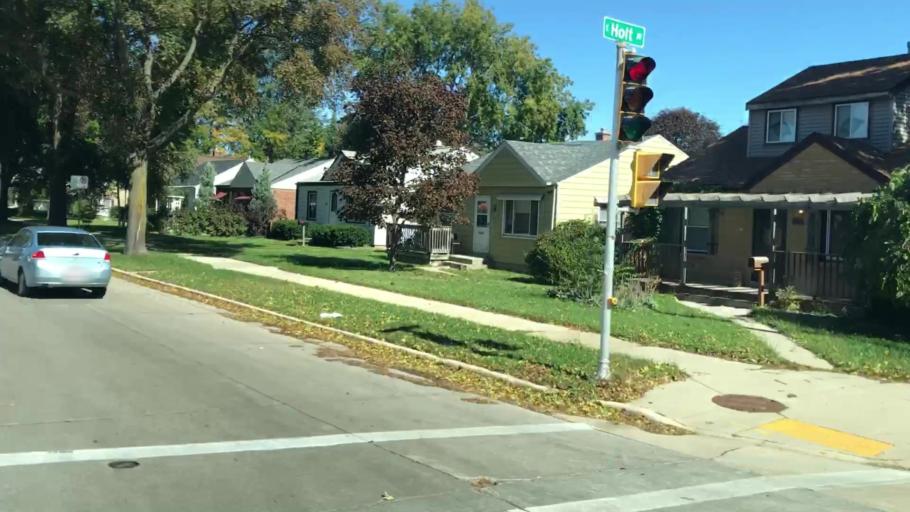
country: US
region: Wisconsin
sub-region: Milwaukee County
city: Saint Francis
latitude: 42.9825
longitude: -87.9093
